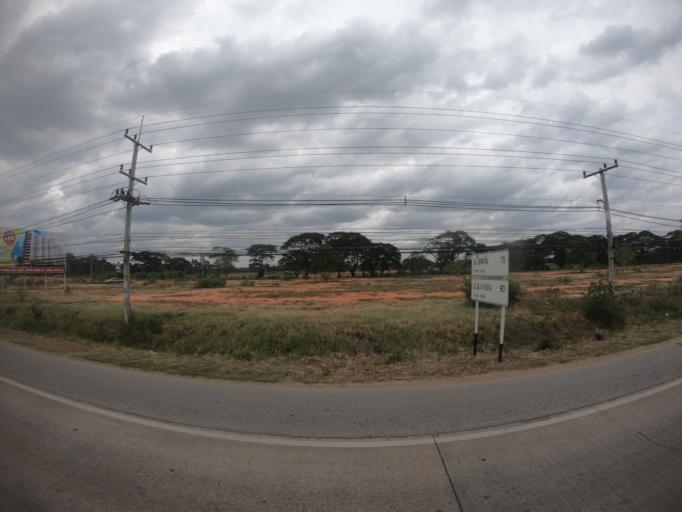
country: TH
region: Nakhon Ratchasima
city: Nakhon Ratchasima
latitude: 14.8657
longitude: 102.1844
